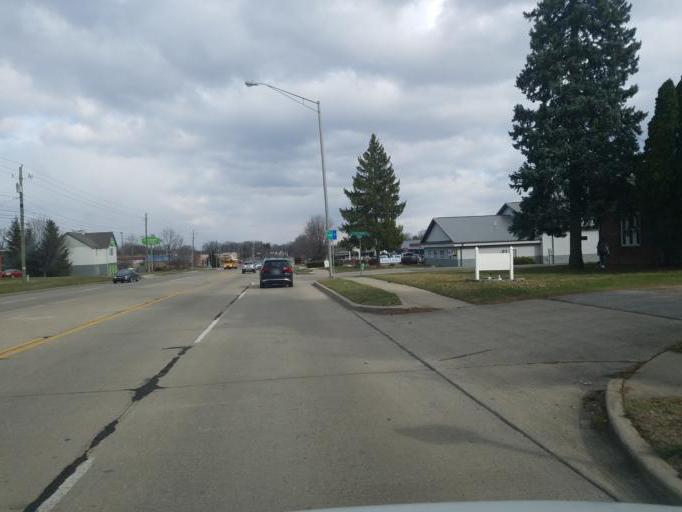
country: US
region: Indiana
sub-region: Marion County
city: Speedway
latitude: 39.7651
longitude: -86.2544
